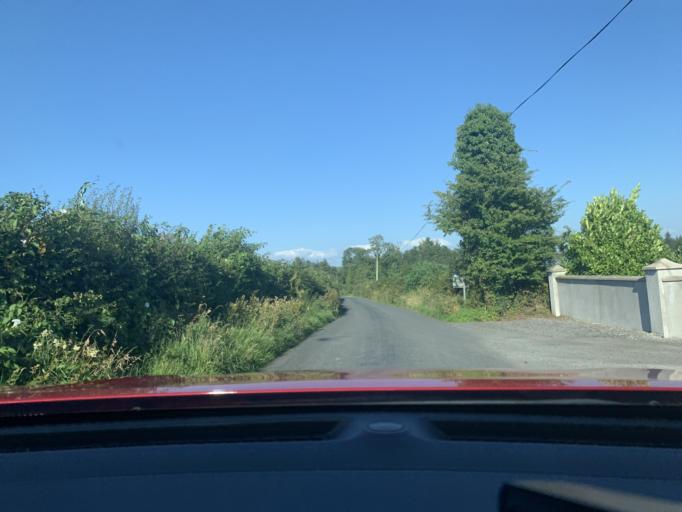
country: IE
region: Connaught
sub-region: Sligo
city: Tobercurry
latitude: 54.0870
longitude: -8.8081
